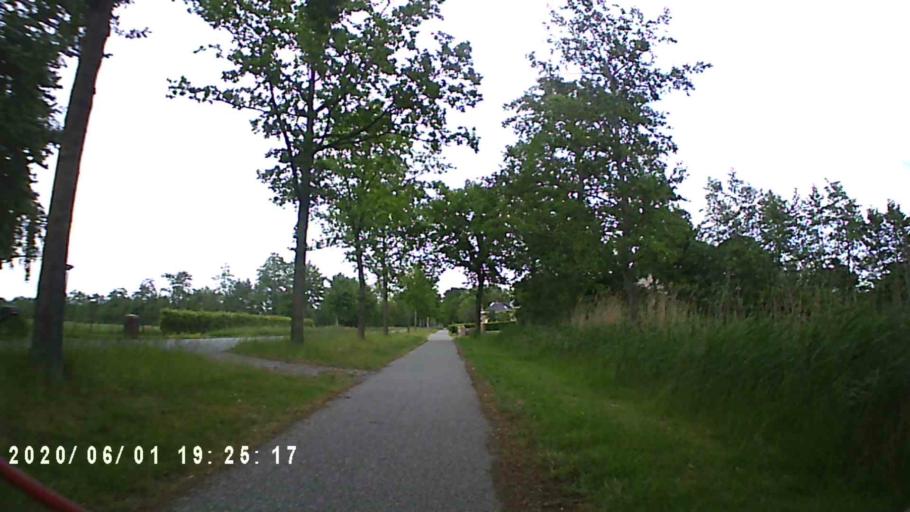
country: NL
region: Friesland
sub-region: Gemeente Achtkarspelen
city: Drogeham
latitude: 53.2075
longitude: 6.1325
